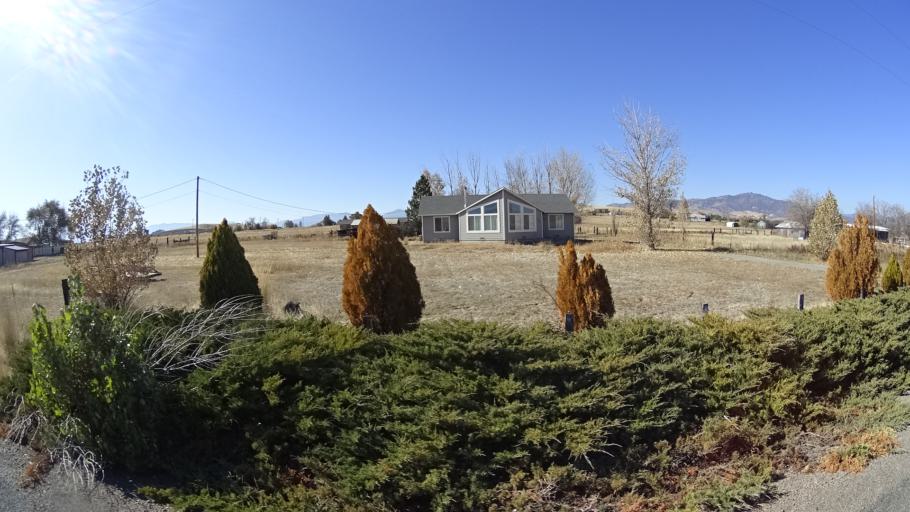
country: US
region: California
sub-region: Siskiyou County
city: Montague
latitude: 41.7572
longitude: -122.4572
